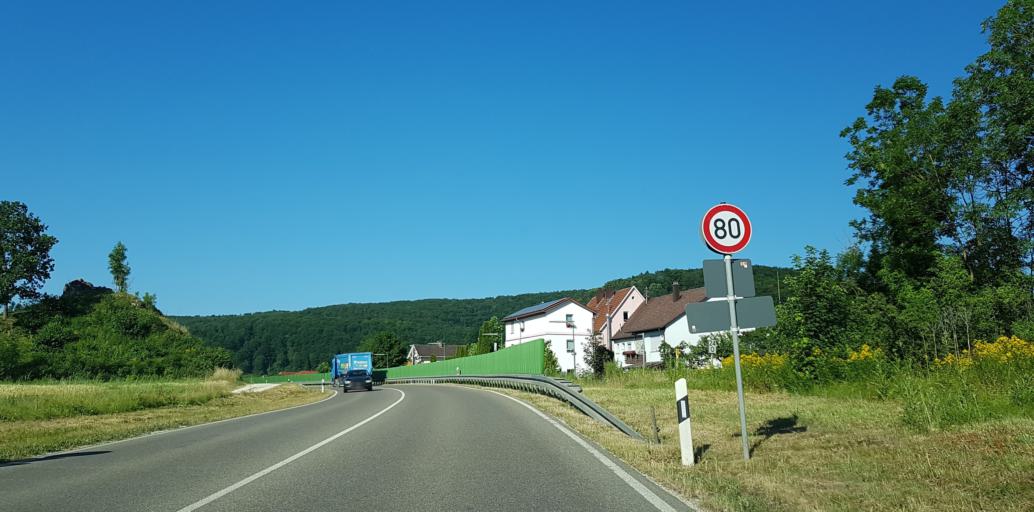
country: DE
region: Baden-Wuerttemberg
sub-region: Tuebingen Region
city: Schelklingen
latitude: 48.3634
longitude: 9.7224
